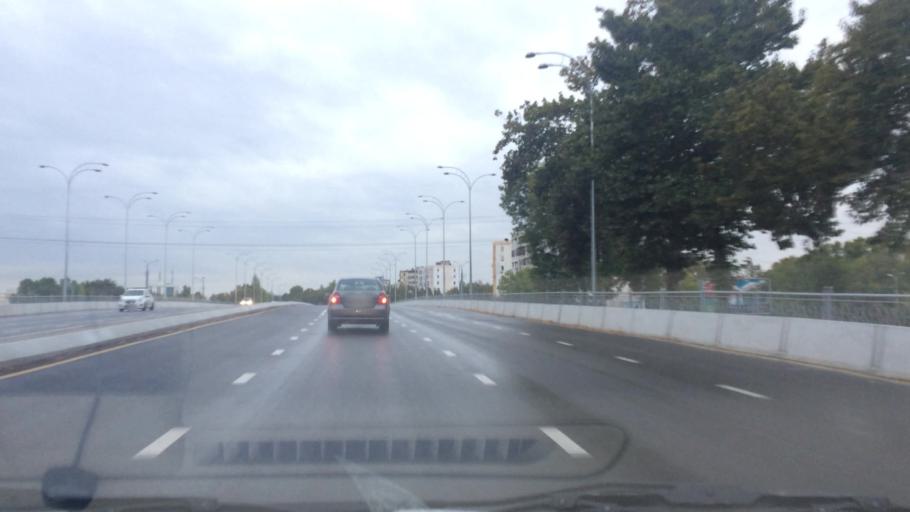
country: UZ
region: Toshkent Shahri
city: Tashkent
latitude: 41.2758
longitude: 69.2057
